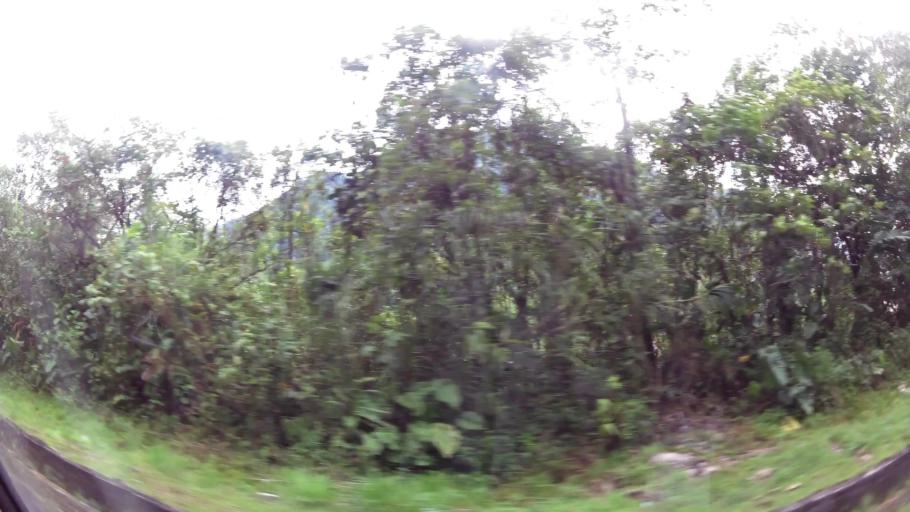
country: EC
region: Pastaza
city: Puyo
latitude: -1.4200
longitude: -78.1755
